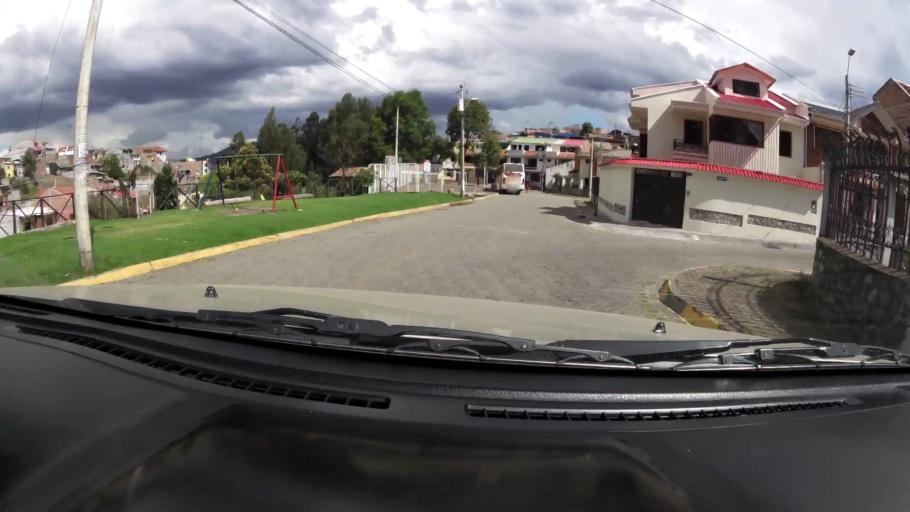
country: EC
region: Azuay
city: Cuenca
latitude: -2.8826
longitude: -78.9814
